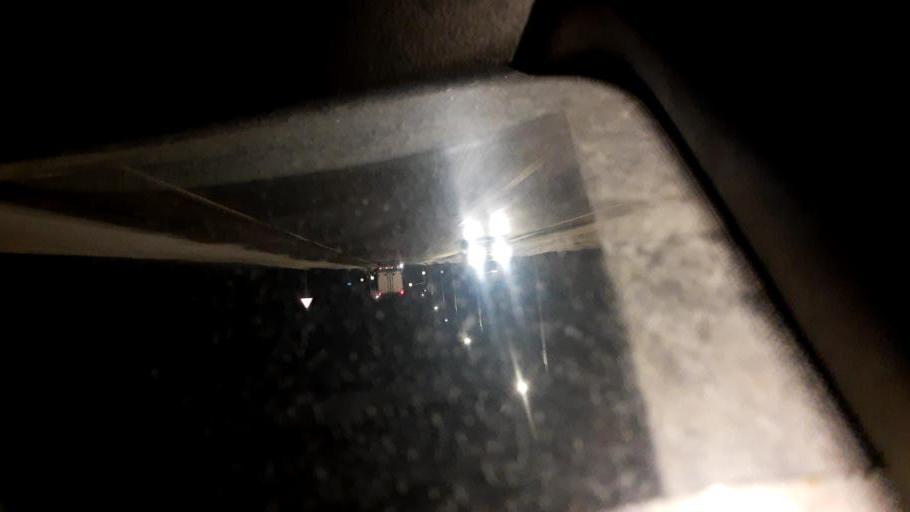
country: RU
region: Moskovskaya
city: Skoropuskovskiy
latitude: 56.3845
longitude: 38.1076
